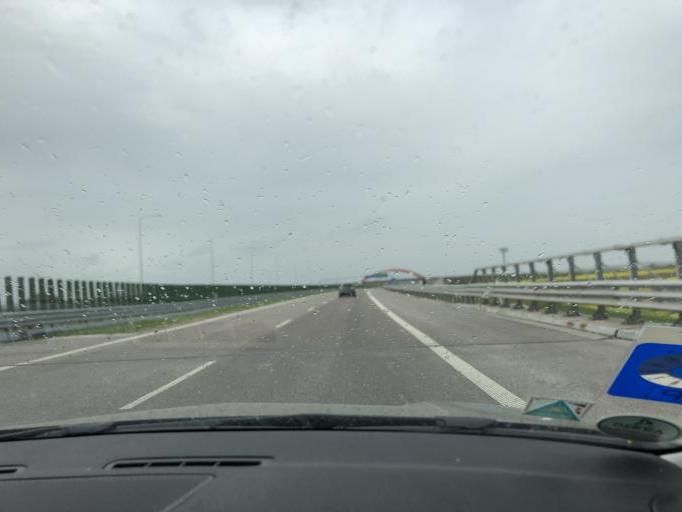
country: PL
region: Subcarpathian Voivodeship
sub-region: Powiat jaroslawski
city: Radymno
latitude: 49.9105
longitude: 22.8183
